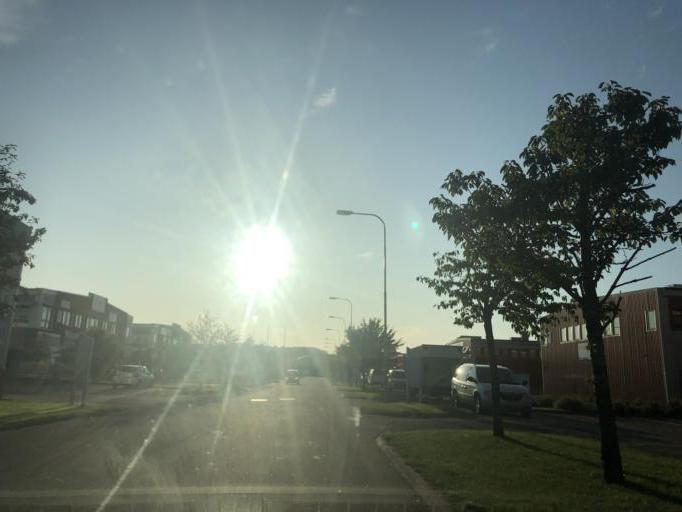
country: SE
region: Vaestra Goetaland
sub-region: Goteborg
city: Eriksbo
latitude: 57.7477
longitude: 12.0002
